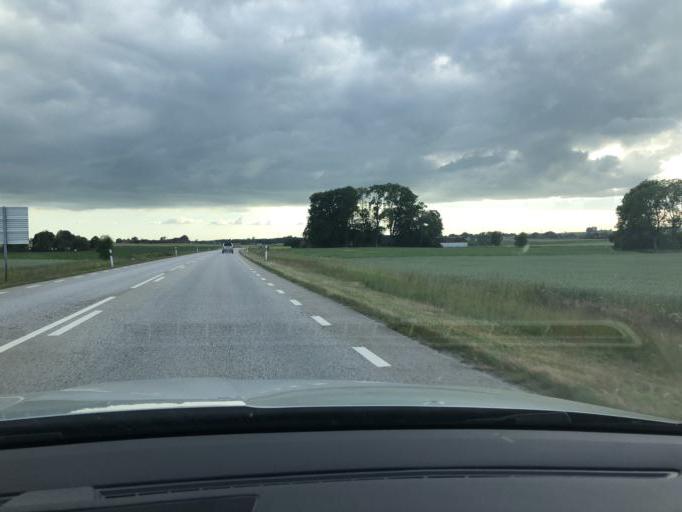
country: SE
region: Skane
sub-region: Simrishamns Kommun
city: Simrishamn
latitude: 55.5374
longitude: 14.3165
